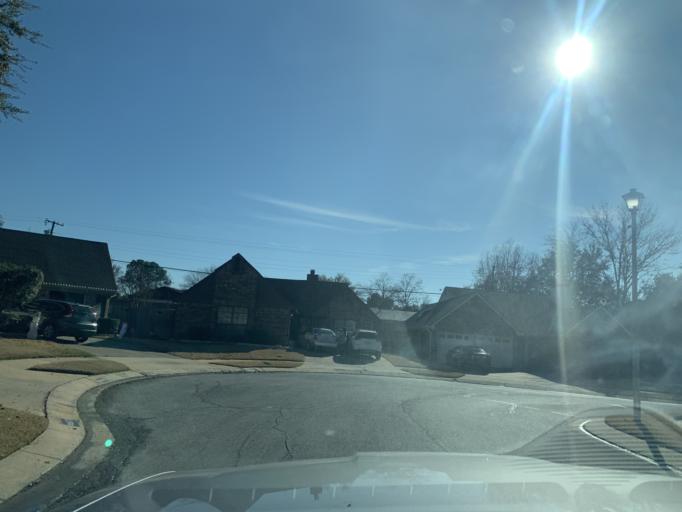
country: US
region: Texas
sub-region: Tarrant County
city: Bedford
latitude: 32.8312
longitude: -97.1378
